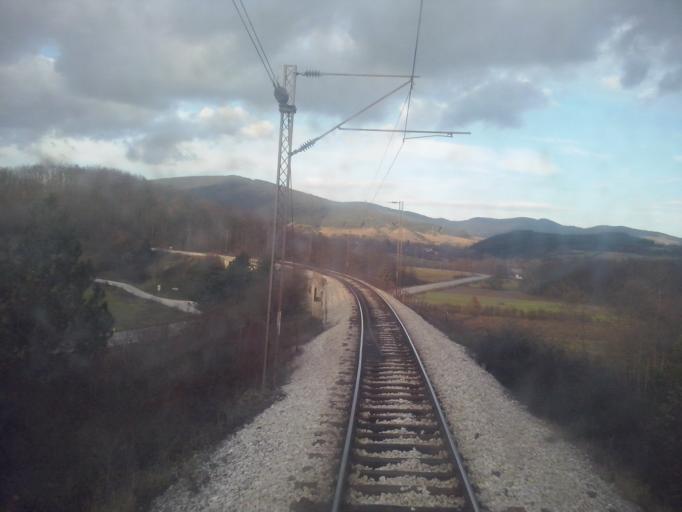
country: RS
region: Central Serbia
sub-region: Zlatiborski Okrug
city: Kosjeric
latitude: 44.0509
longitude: 19.9201
